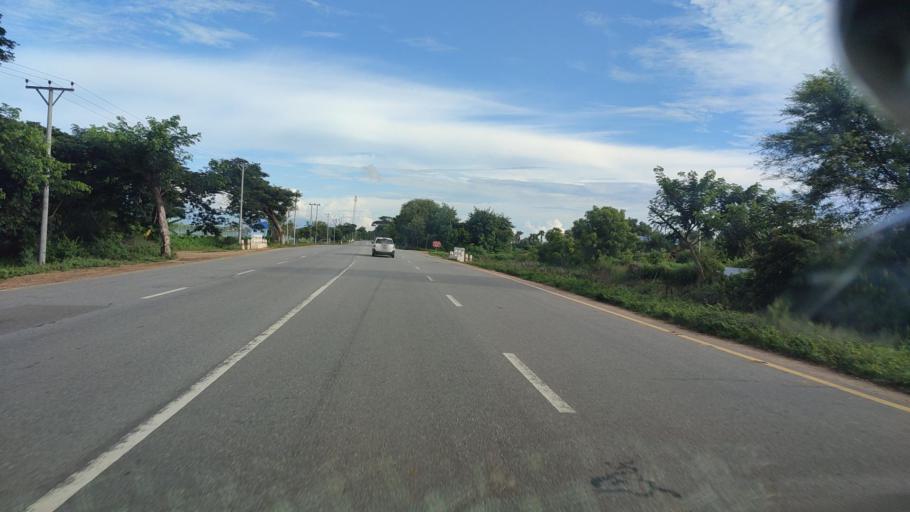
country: MM
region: Mandalay
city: Yamethin
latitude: 20.2021
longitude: 96.1809
